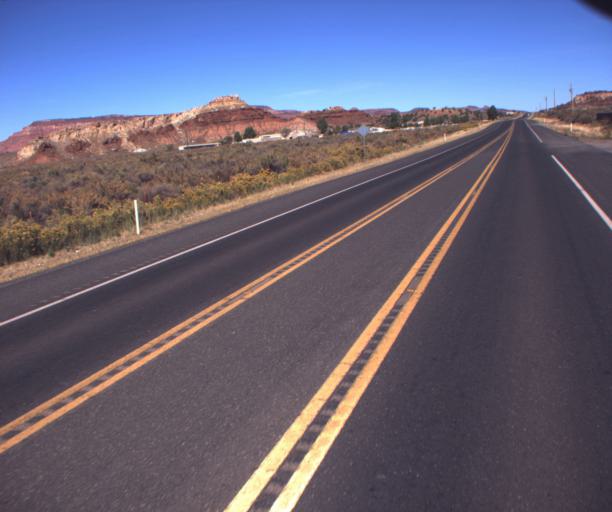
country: US
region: Arizona
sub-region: Coconino County
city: Fredonia
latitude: 36.9754
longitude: -112.5282
